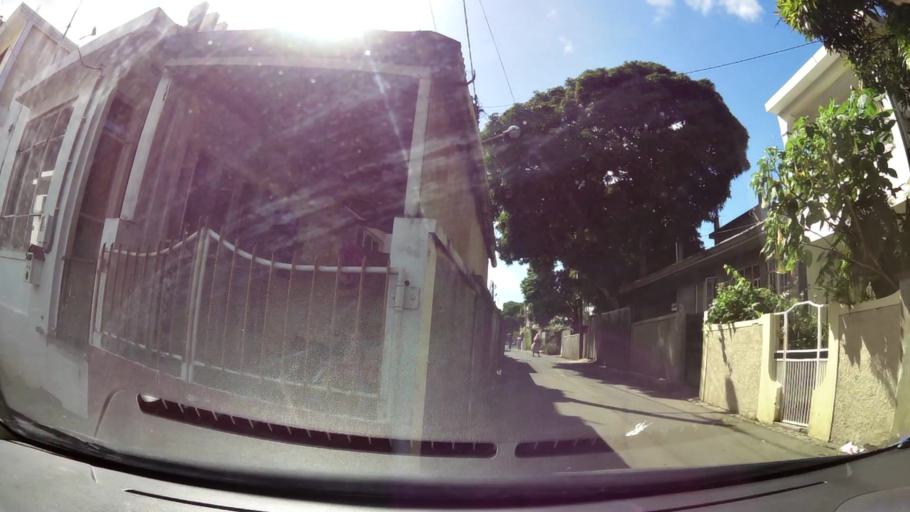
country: MU
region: Grand Port
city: Plaine Magnien
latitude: -20.4294
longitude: 57.6572
